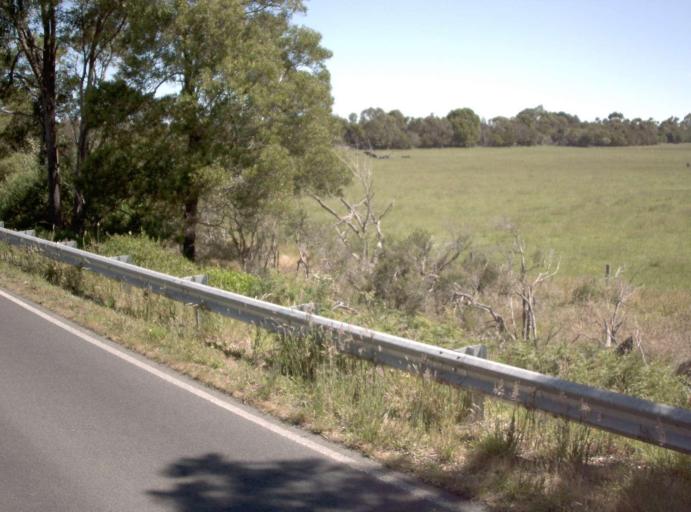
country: AU
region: Victoria
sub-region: Latrobe
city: Morwell
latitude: -38.6662
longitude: 146.1934
